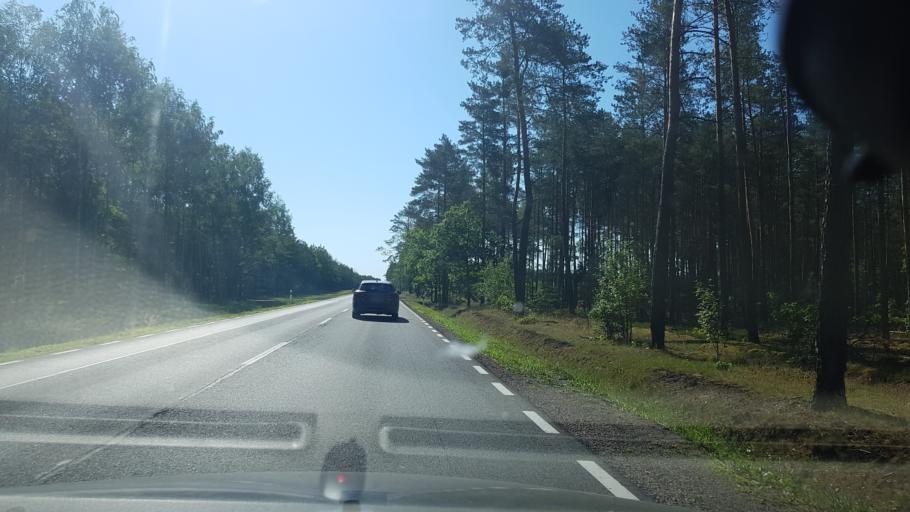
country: PL
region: Masovian Voivodeship
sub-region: Powiat wyszkowski
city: Branszczyk
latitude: 52.5638
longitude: 21.5629
